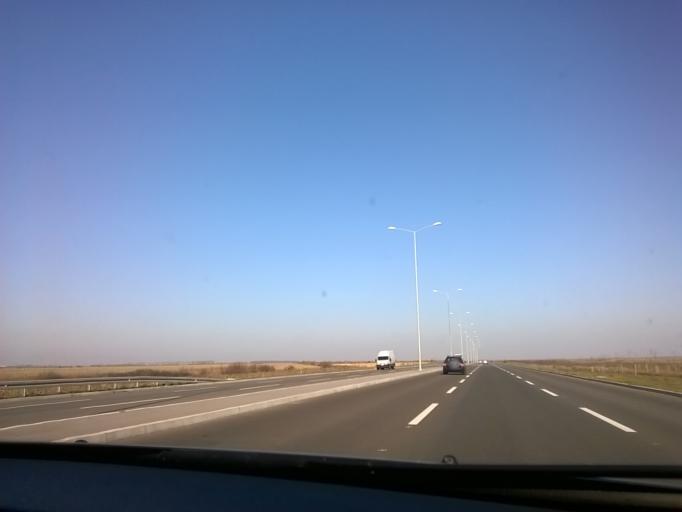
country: RS
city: Ovca
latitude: 44.8900
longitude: 20.5174
